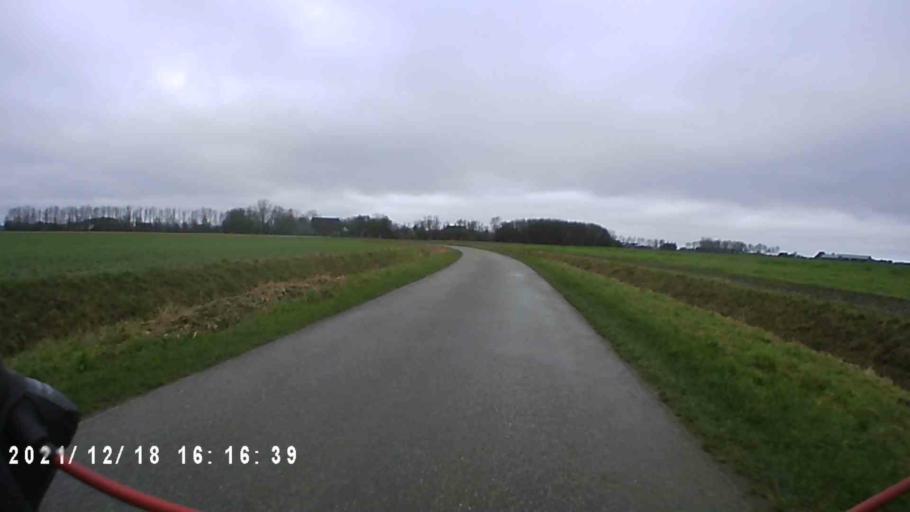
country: NL
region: Friesland
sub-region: Gemeente Dongeradeel
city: Anjum
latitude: 53.3730
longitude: 6.0597
